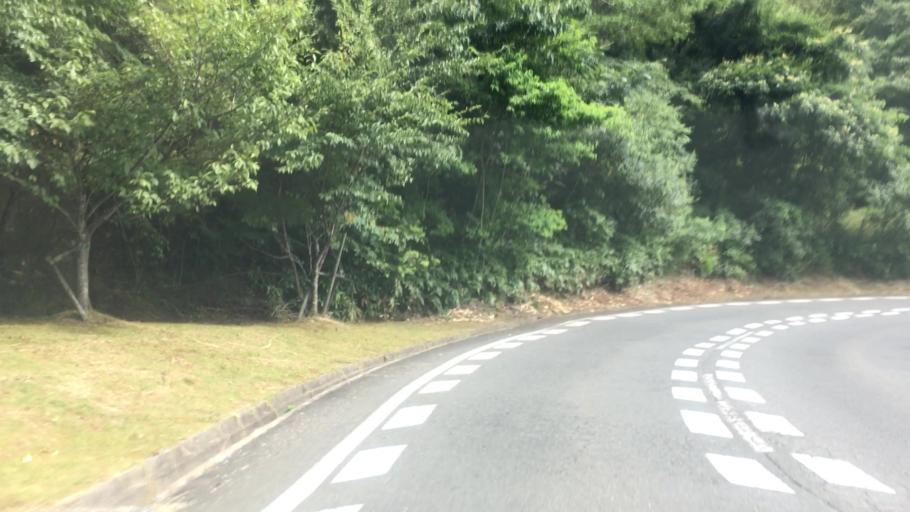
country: JP
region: Hyogo
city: Toyooka
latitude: 35.5216
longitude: 134.7905
